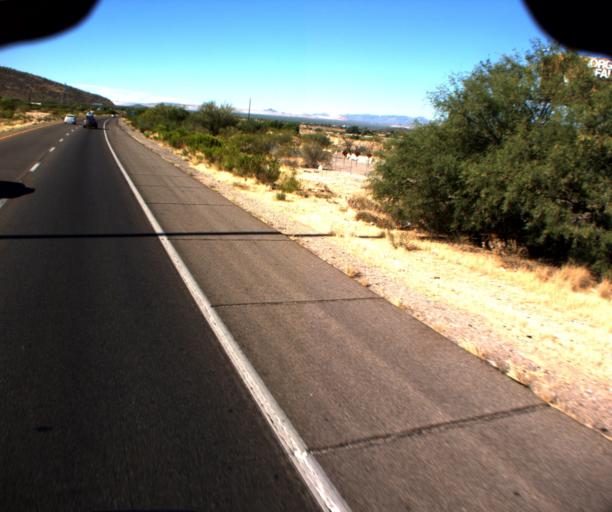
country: US
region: Arizona
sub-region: Pima County
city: Drexel Heights
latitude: 32.1259
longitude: -110.9872
